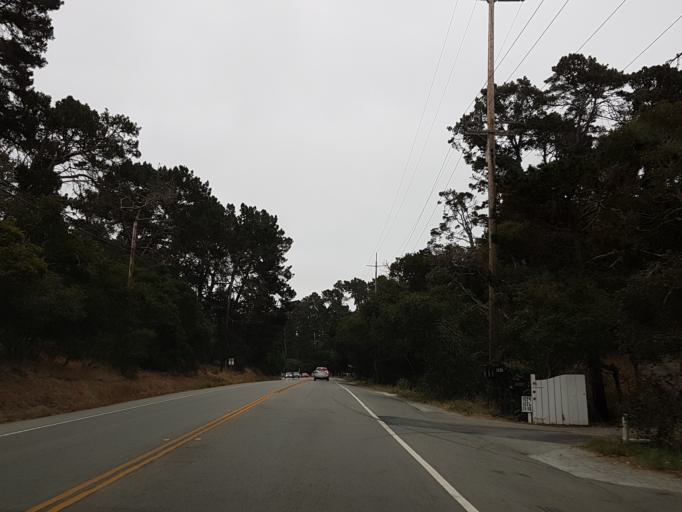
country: US
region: California
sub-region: Monterey County
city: Del Rey Oaks
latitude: 36.5848
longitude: -121.8596
